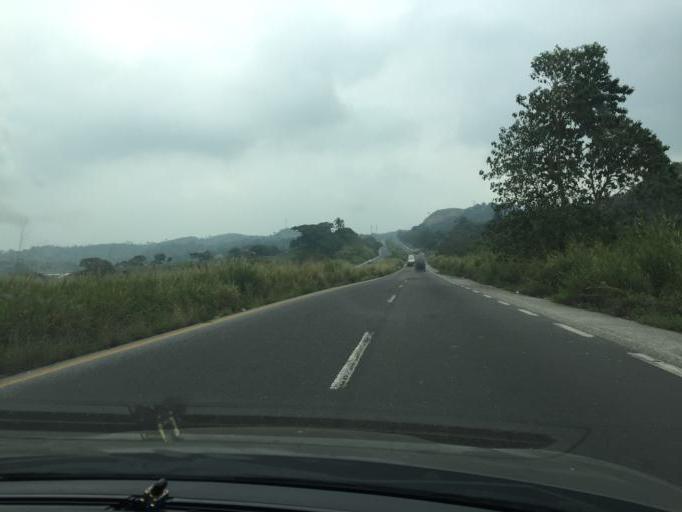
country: MX
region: Veracruz
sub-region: Moloacan
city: Tlacuilolapan
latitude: 18.0743
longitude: -94.2815
